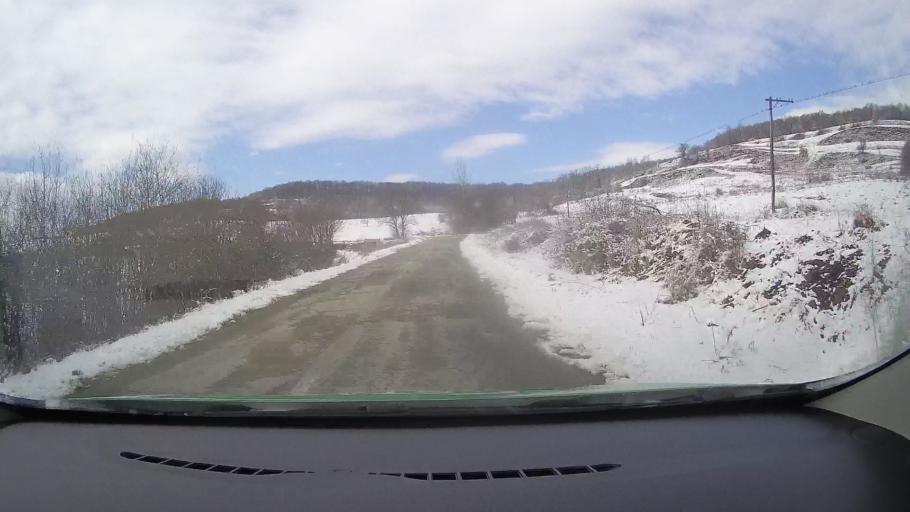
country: RO
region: Sibiu
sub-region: Comuna Altina
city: Altina
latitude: 45.9948
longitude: 24.4416
